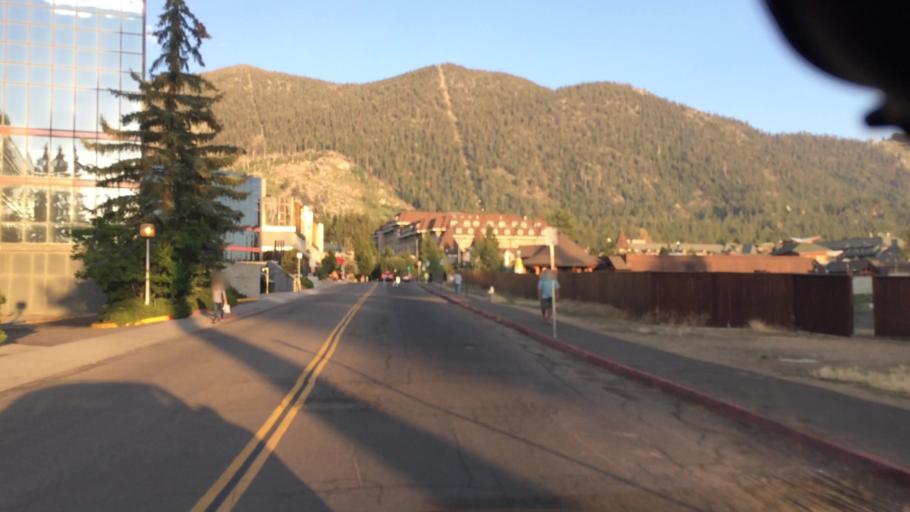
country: US
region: Nevada
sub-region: Douglas County
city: Kingsbury
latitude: 38.9603
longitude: -119.9439
